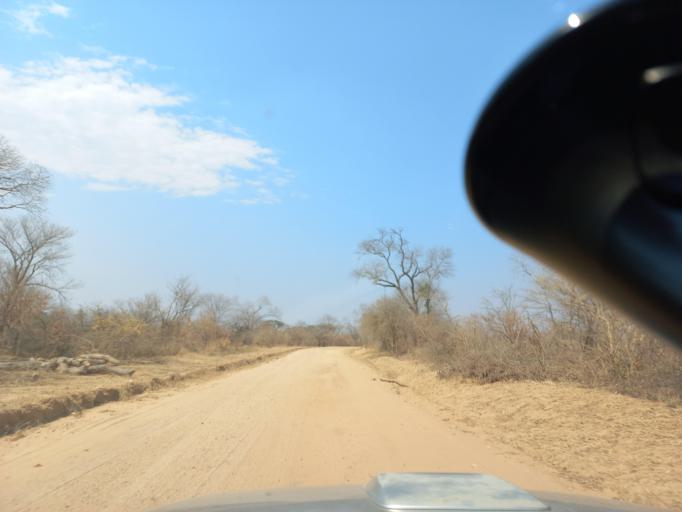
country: ZW
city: Chirundu
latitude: -15.9248
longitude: 28.8871
